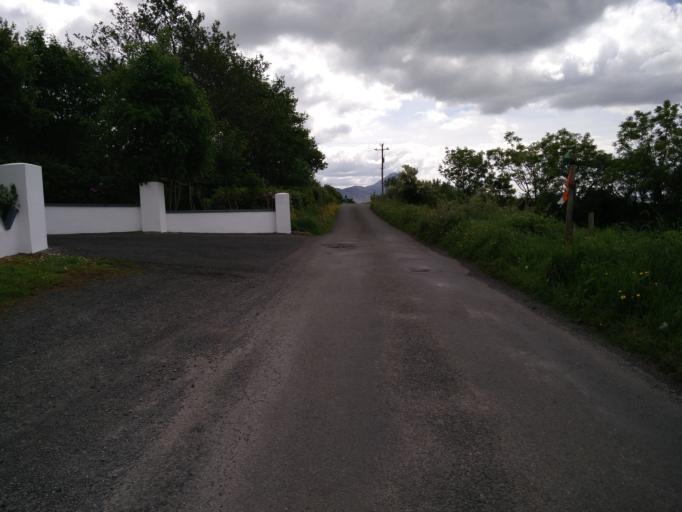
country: IE
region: Connaught
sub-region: Maigh Eo
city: Westport
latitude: 53.8168
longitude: -9.5189
